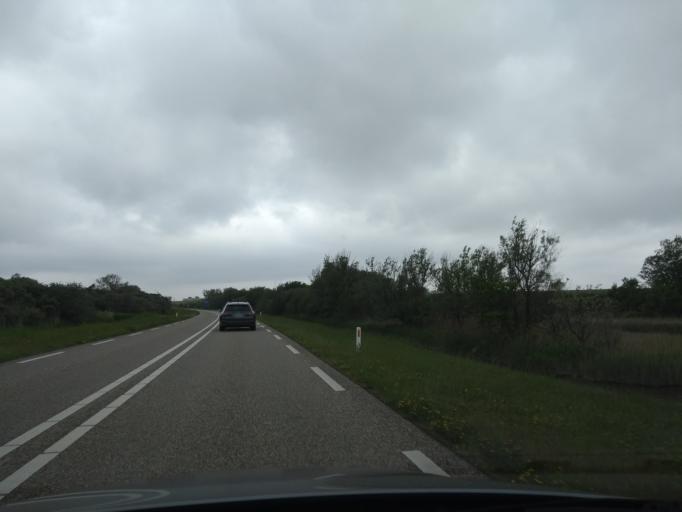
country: NL
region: Friesland
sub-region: Gemeente Dongeradeel
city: Anjum
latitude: 53.4072
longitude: 6.2202
